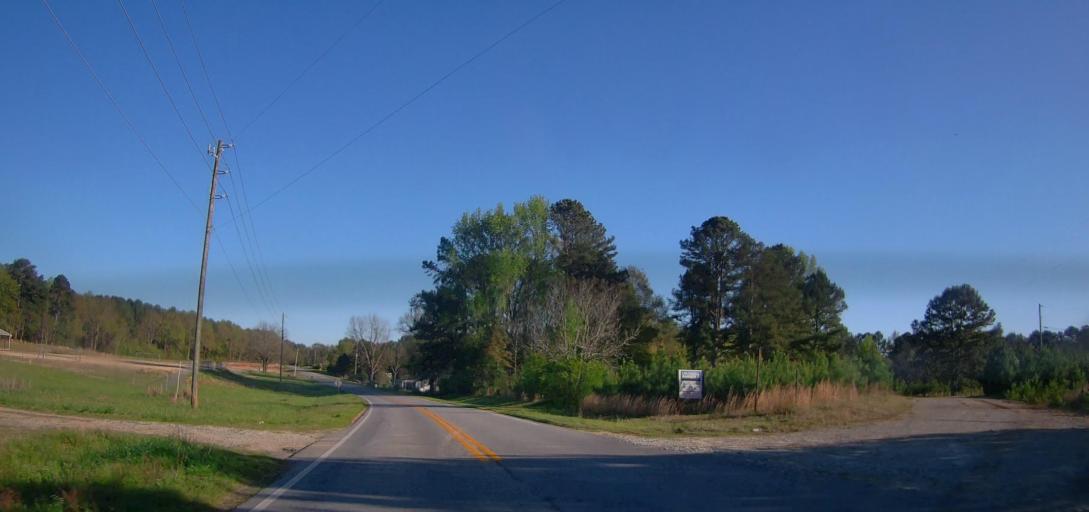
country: US
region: Georgia
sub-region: Butts County
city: Jackson
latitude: 33.3295
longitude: -83.9067
